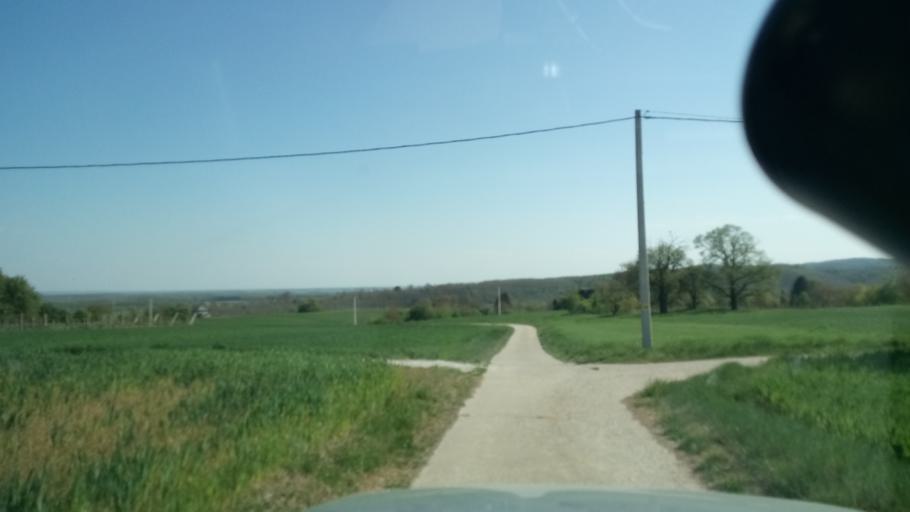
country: HU
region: Zala
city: Sarmellek
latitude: 46.7026
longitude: 17.0967
